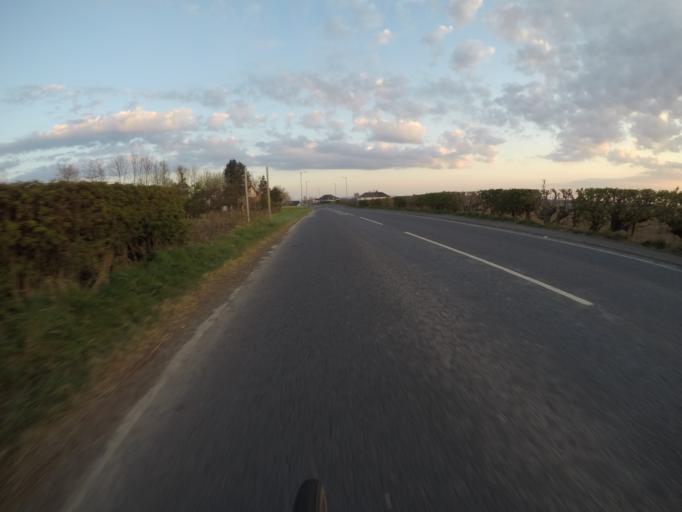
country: GB
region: Scotland
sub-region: South Ayrshire
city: Troon
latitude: 55.5542
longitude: -4.6261
